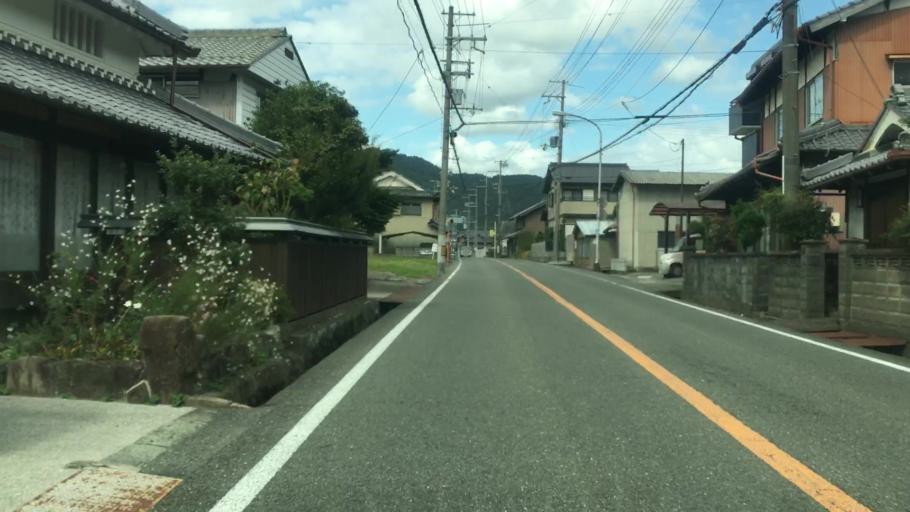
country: JP
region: Kyoto
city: Fukuchiyama
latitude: 35.1468
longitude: 135.0655
